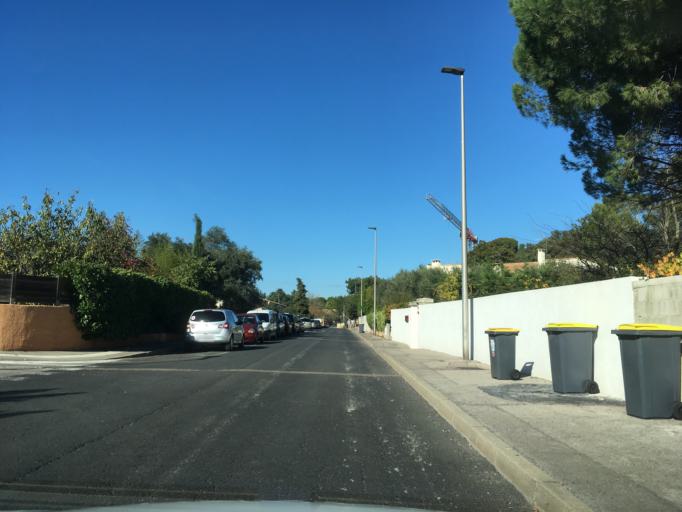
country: FR
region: Languedoc-Roussillon
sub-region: Departement de l'Herault
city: Juvignac
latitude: 43.6052
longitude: 3.8337
